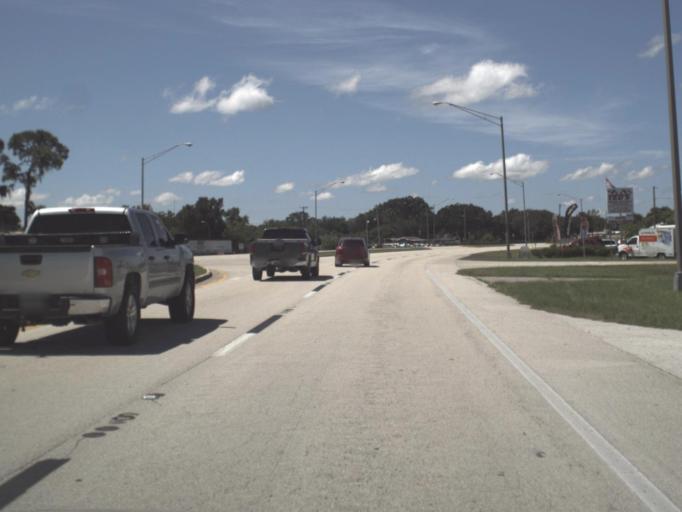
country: US
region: Florida
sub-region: Polk County
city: Auburndale
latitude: 28.0602
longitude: -81.7775
